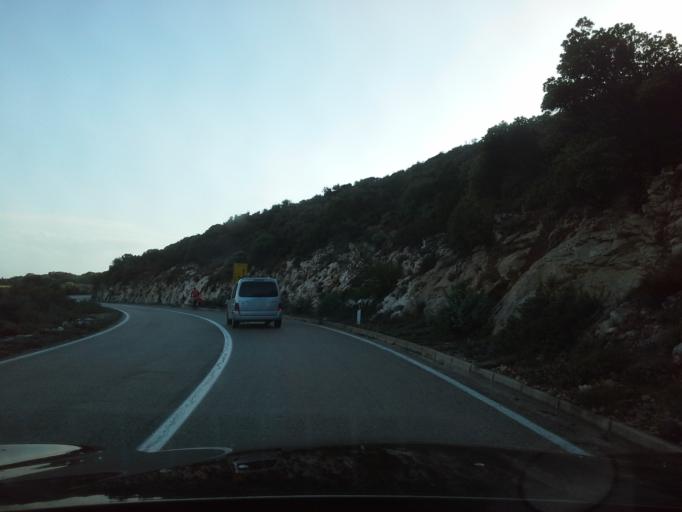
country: HR
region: Primorsko-Goranska
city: Mali Losinj
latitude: 44.5964
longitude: 14.4089
